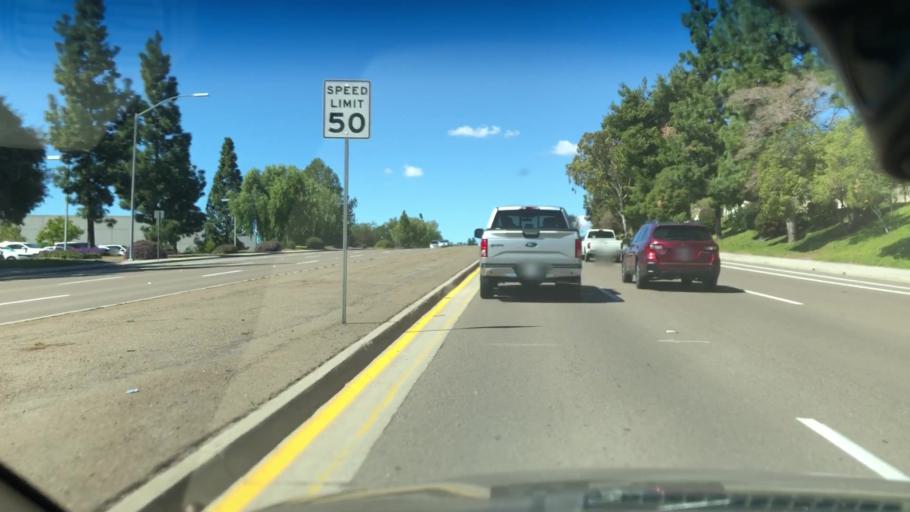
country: US
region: California
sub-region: San Diego County
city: Poway
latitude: 32.9882
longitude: -117.0677
